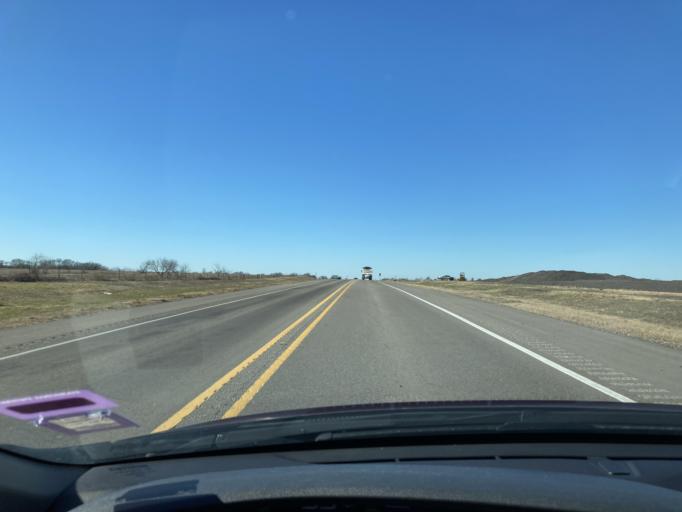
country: US
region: Texas
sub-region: Navarro County
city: Corsicana
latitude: 32.0480
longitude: -96.4823
